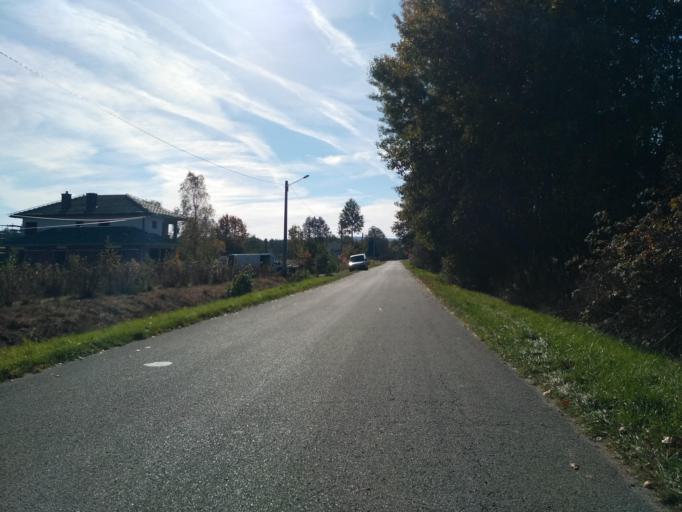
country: PL
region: Subcarpathian Voivodeship
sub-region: Powiat rzeszowski
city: Trzciana
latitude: 50.0863
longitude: 21.8136
